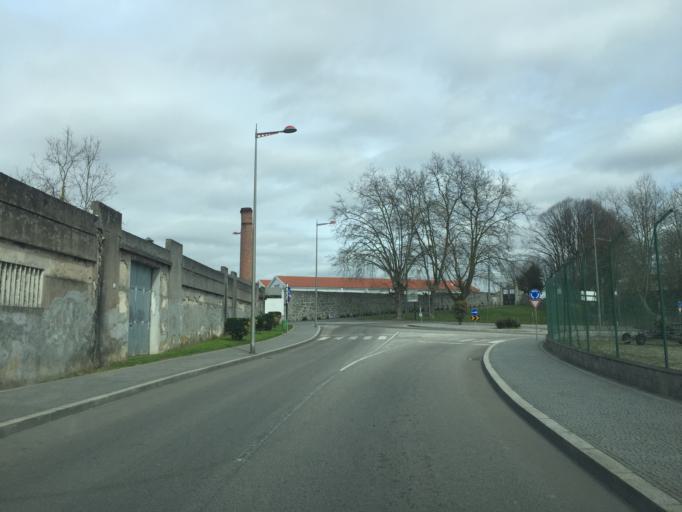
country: PT
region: Porto
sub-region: Vila Nova de Gaia
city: Vila Nova de Gaia
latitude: 41.1373
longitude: -8.6044
